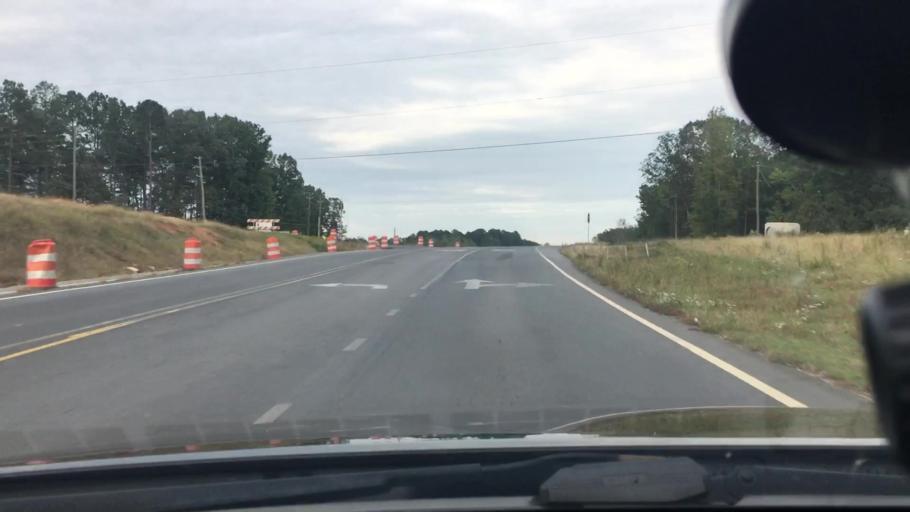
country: US
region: North Carolina
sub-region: Montgomery County
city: Troy
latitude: 35.3320
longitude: -79.9316
